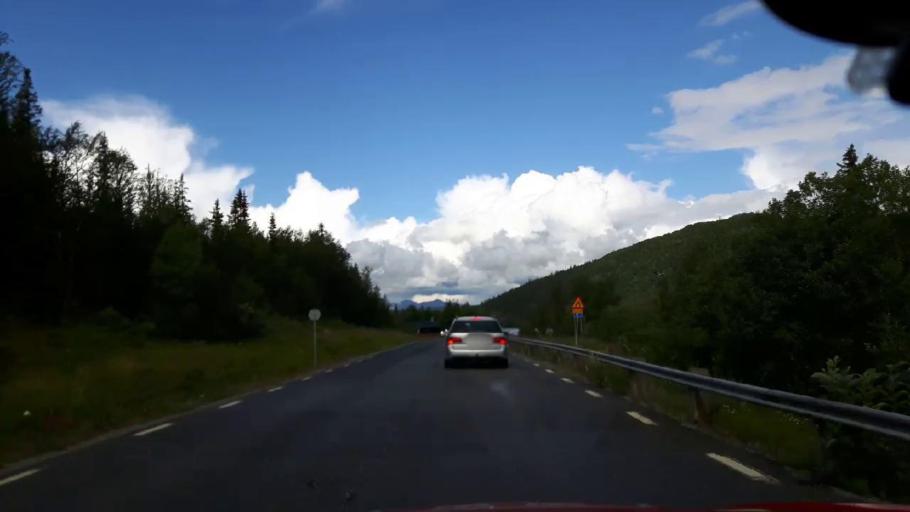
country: SE
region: Vaesterbotten
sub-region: Vilhelmina Kommun
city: Sjoberg
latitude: 65.0296
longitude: 15.1409
